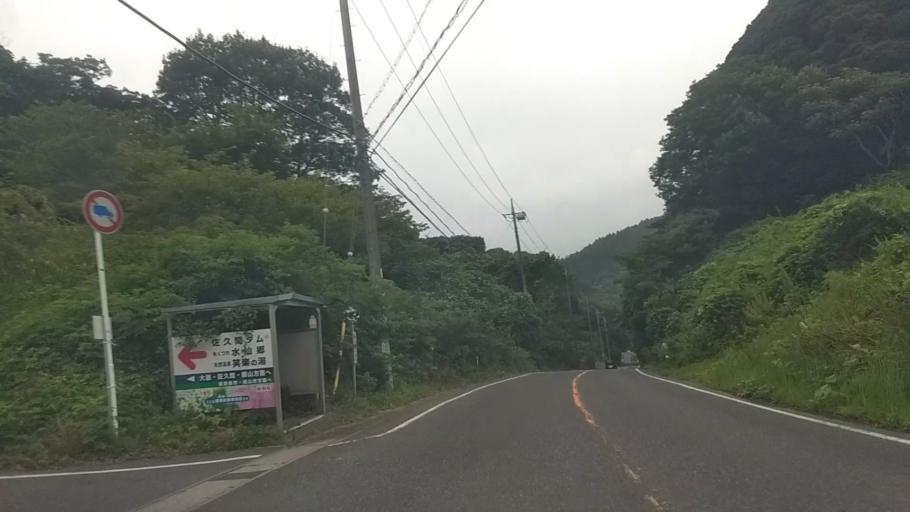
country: JP
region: Chiba
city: Tateyama
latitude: 35.1395
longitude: 139.9041
